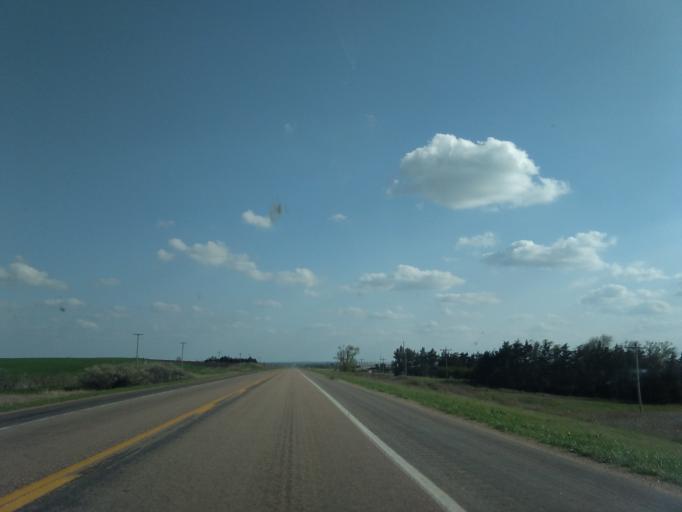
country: US
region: Nebraska
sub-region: Webster County
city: Red Cloud
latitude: 40.1455
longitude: -98.5191
